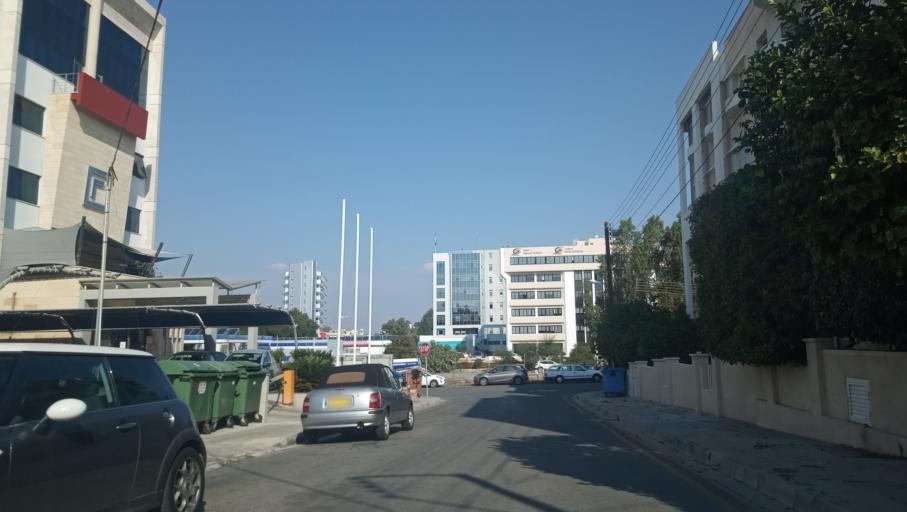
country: CY
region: Lefkosia
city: Nicosia
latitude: 35.1523
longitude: 33.3755
